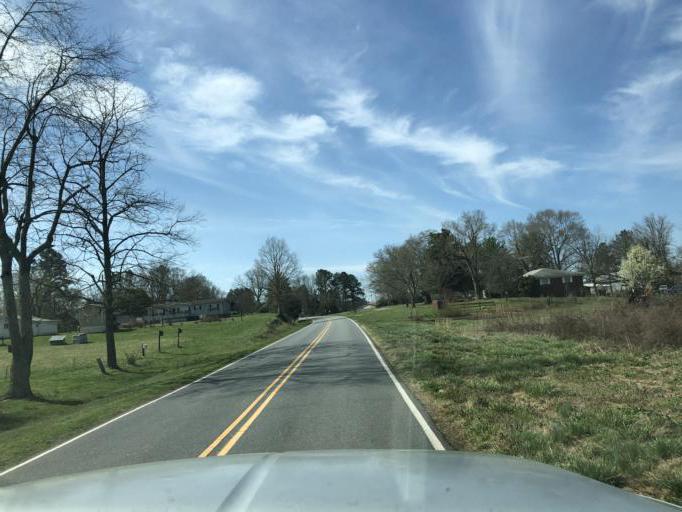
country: US
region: North Carolina
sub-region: Cleveland County
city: Shelby
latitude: 35.4246
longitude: -81.6438
